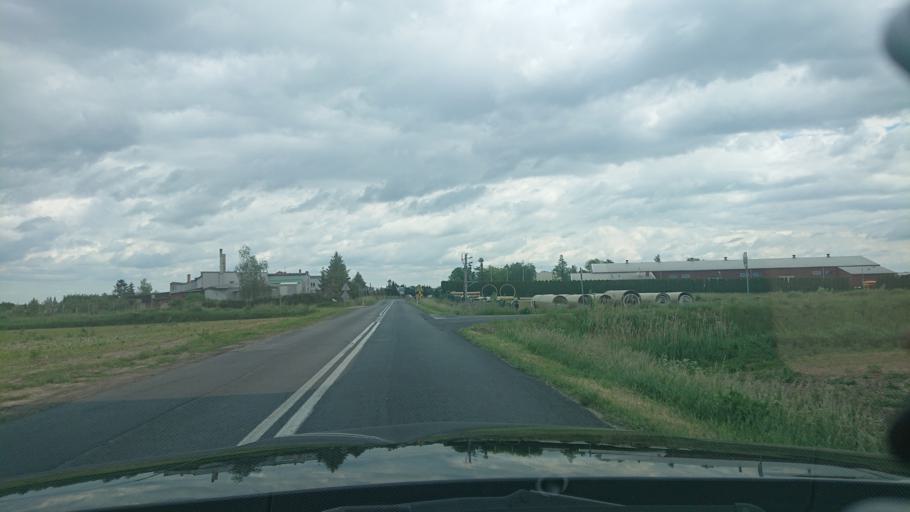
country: PL
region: Greater Poland Voivodeship
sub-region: Powiat gnieznienski
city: Gniezno
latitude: 52.5349
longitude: 17.5431
